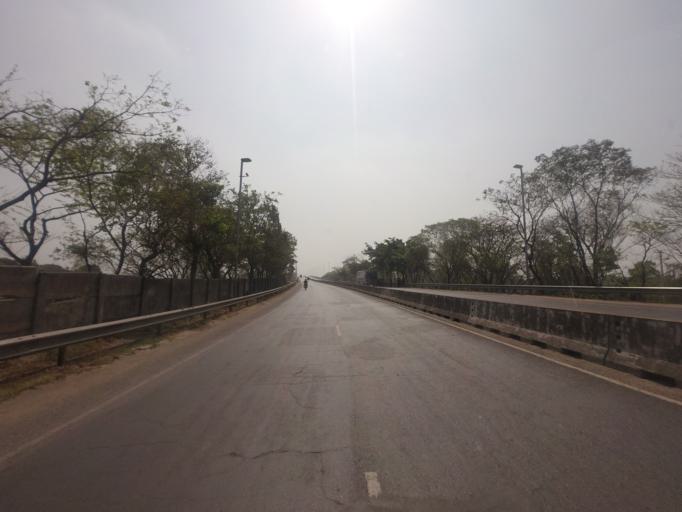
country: BD
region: Dhaka
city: Bhairab Bazar
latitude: 24.0497
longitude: 90.9909
